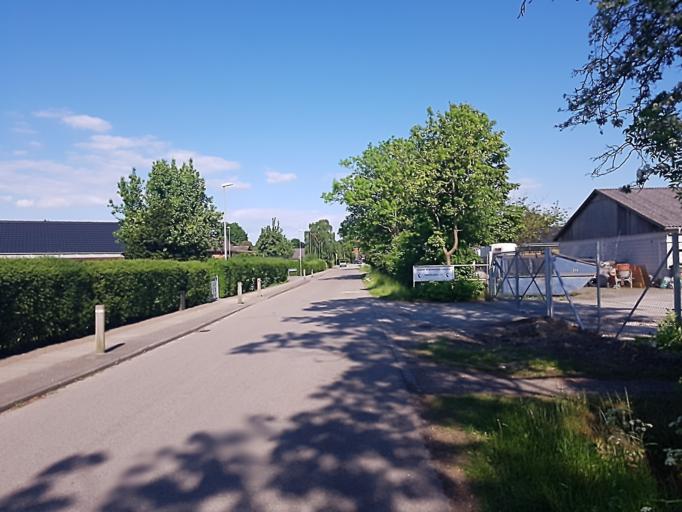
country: DK
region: Capital Region
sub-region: Tarnby Kommune
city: Tarnby
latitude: 55.6274
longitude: 12.5956
